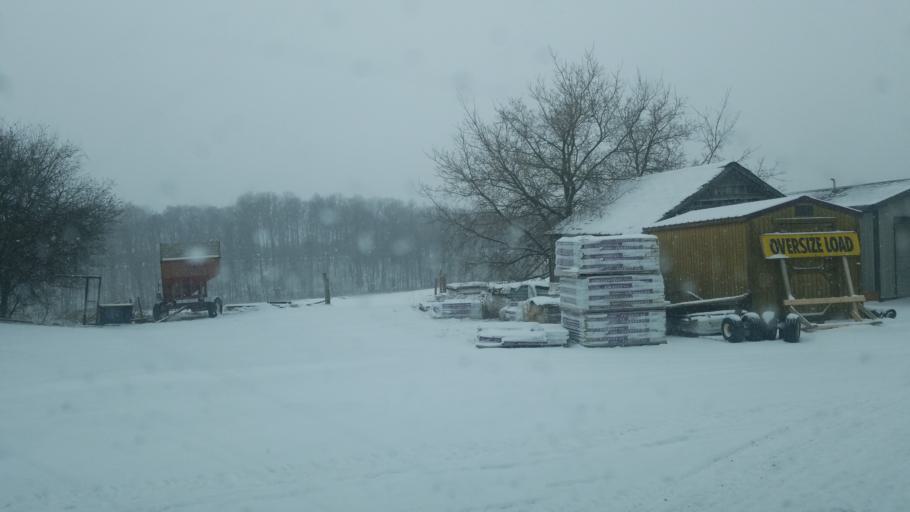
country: US
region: Michigan
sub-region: Osceola County
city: Reed City
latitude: 43.8422
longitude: -85.4063
